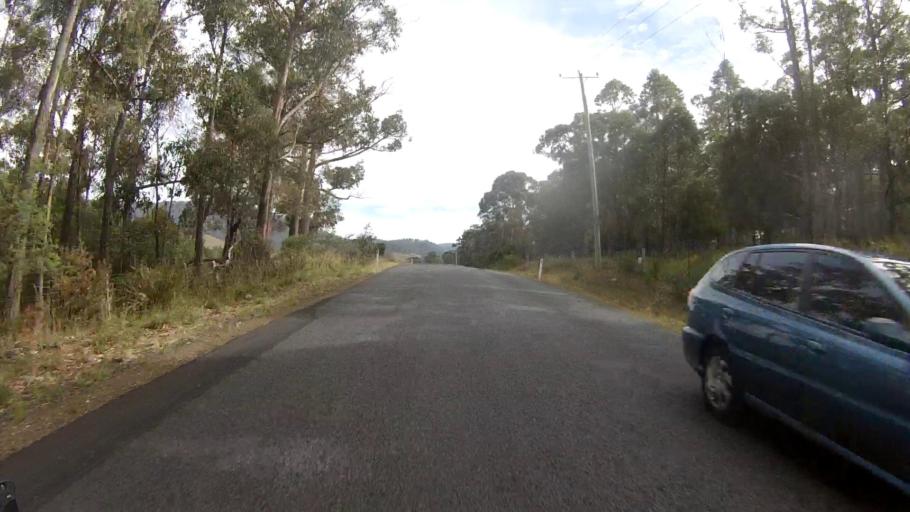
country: AU
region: Tasmania
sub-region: Sorell
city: Sorell
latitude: -42.8016
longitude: 147.7934
